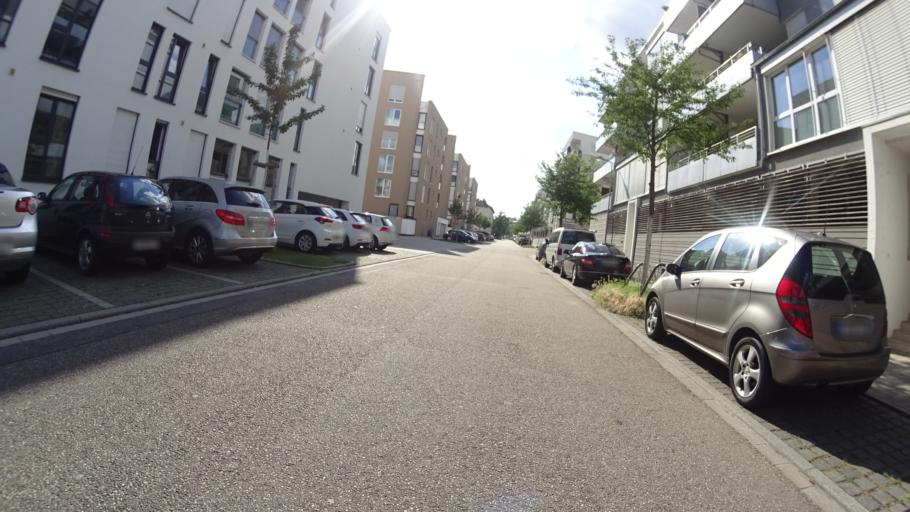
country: DE
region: Baden-Wuerttemberg
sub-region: Karlsruhe Region
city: Karlsruhe
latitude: 49.0004
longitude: 8.4191
